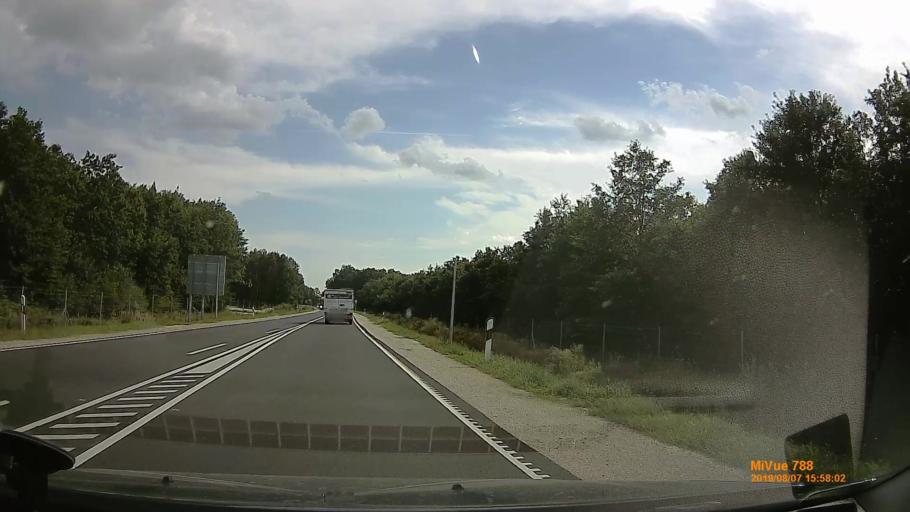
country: HU
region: Vas
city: Kormend
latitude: 47.0320
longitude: 16.6127
